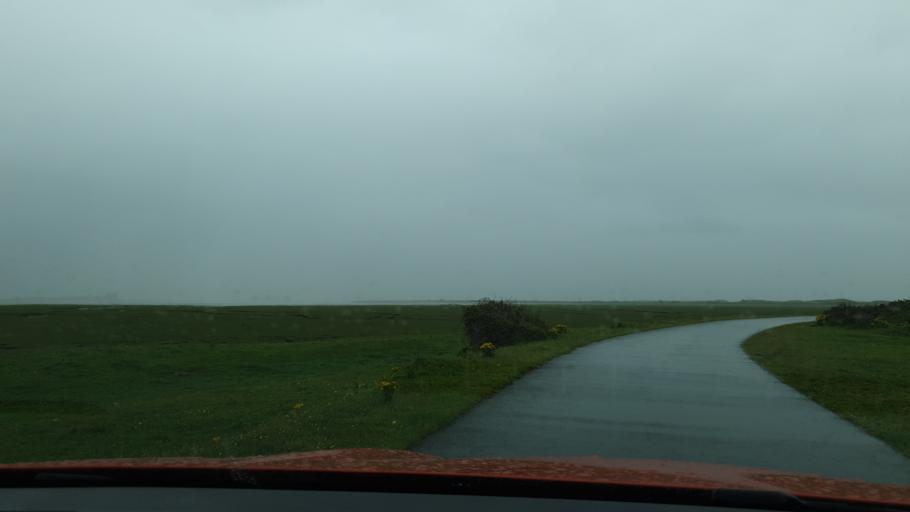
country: GB
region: England
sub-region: Cumbria
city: Barrow in Furness
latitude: 54.0543
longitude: -3.2082
